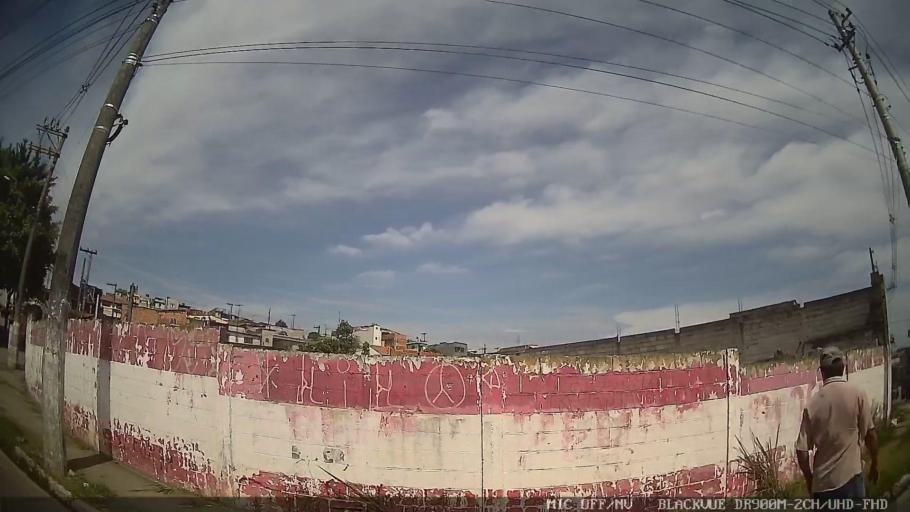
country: BR
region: Sao Paulo
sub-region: Suzano
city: Suzano
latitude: -23.5062
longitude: -46.3000
